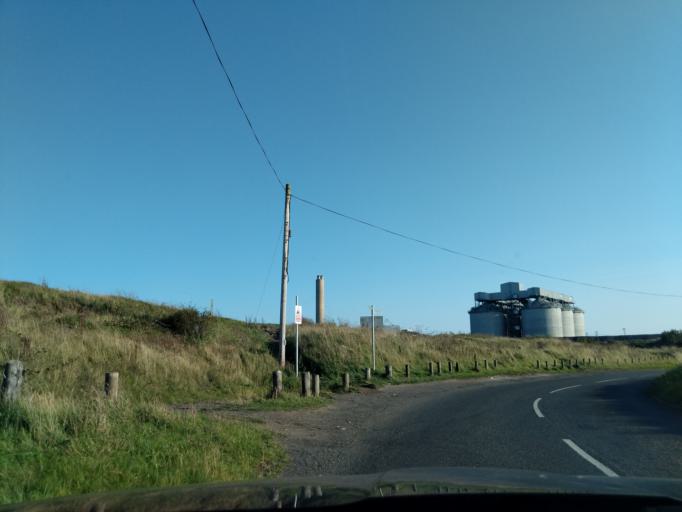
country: GB
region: England
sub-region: Northumberland
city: Lynemouth
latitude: 55.2104
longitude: -1.5265
